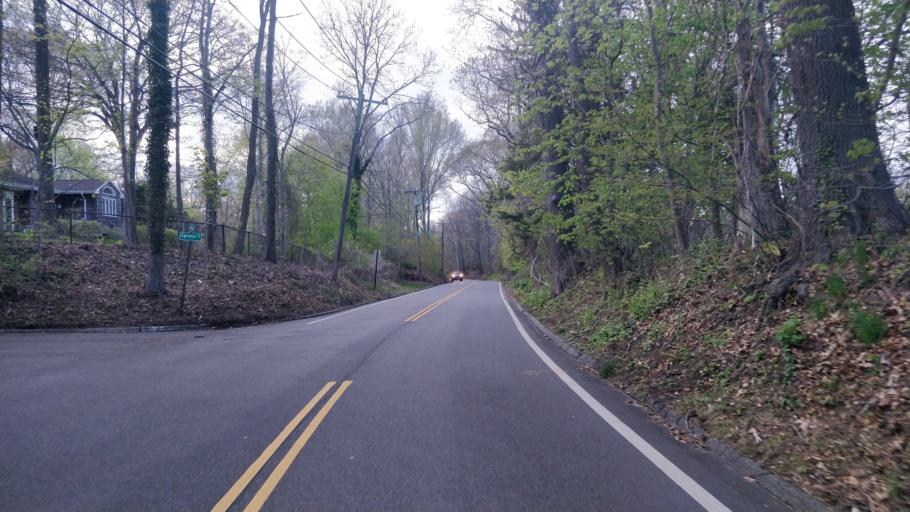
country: US
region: New York
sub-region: Suffolk County
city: Nissequogue
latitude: 40.8848
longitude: -73.2144
